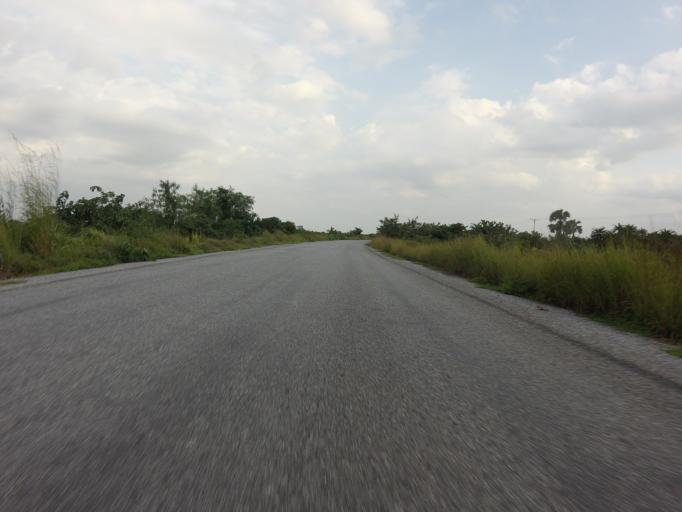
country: GH
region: Volta
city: Ho
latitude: 6.3823
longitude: 0.5309
